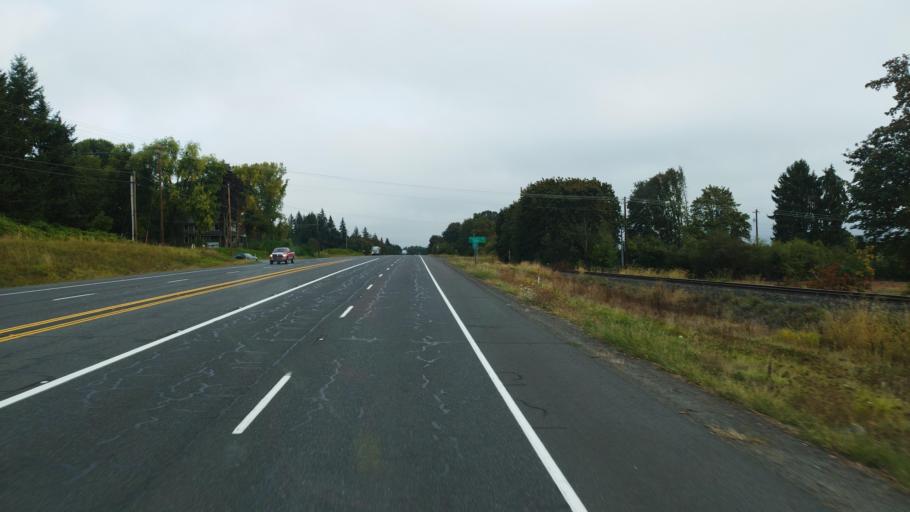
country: US
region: Oregon
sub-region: Columbia County
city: Warren
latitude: 45.7908
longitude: -122.8697
